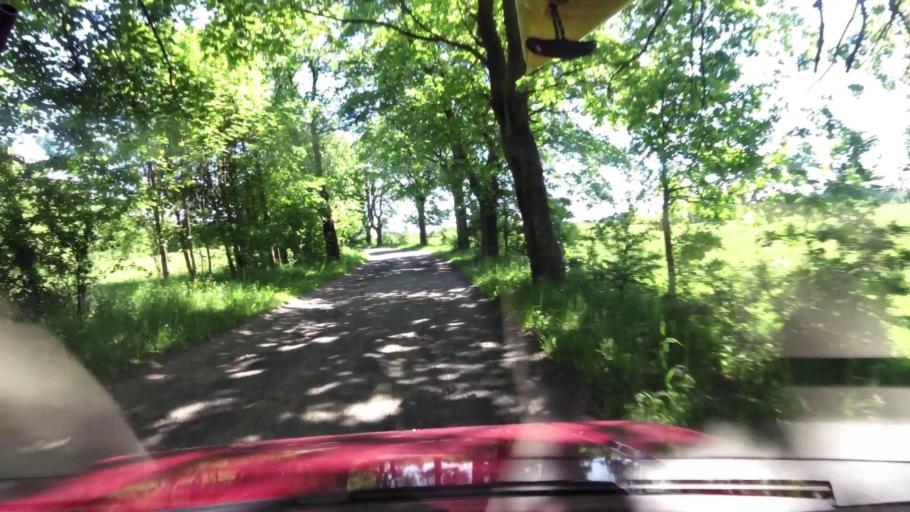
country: PL
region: West Pomeranian Voivodeship
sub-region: Powiat koszalinski
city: Polanow
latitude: 54.0432
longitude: 16.7490
